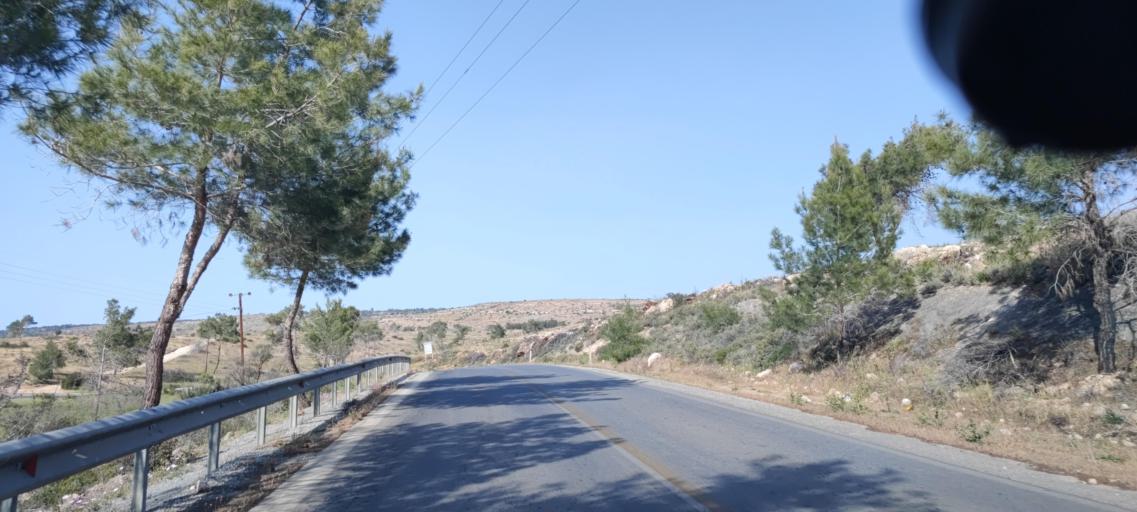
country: CY
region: Lefkosia
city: Morfou
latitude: 35.2657
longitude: 33.0429
